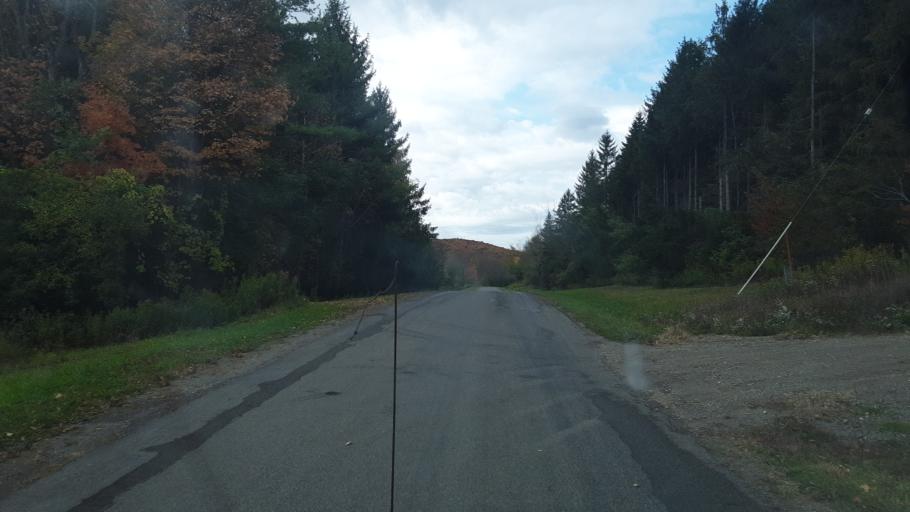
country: US
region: New York
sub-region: Allegany County
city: Alfred
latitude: 42.3645
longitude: -77.8310
